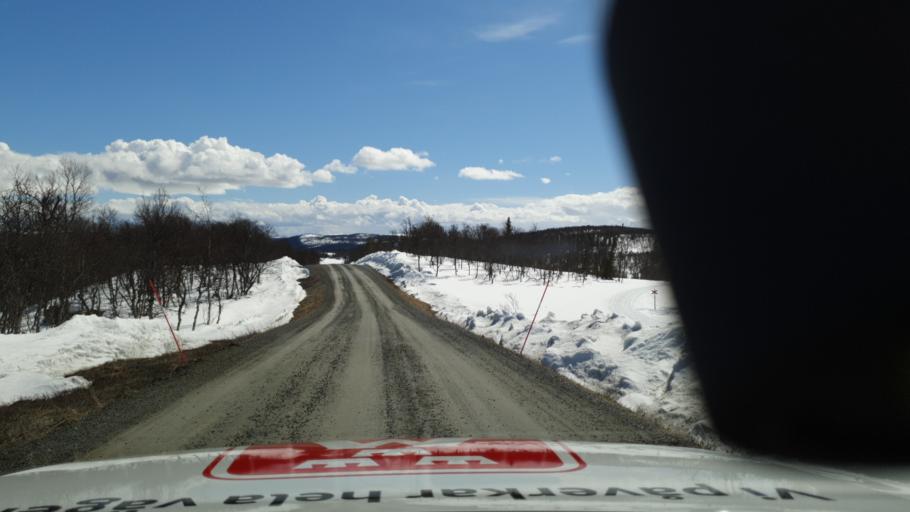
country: SE
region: Jaemtland
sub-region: Are Kommun
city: Are
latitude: 62.8902
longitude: 12.7166
